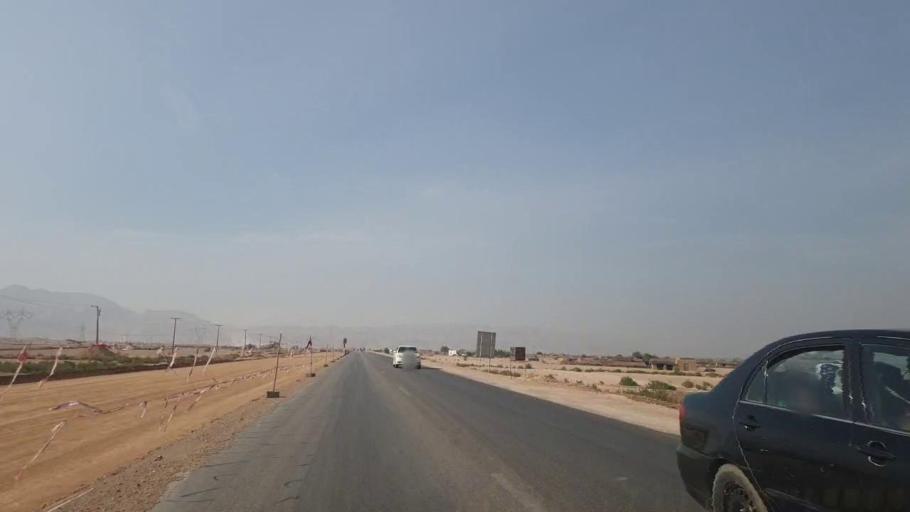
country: PK
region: Sindh
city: Sehwan
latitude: 26.1986
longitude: 67.9413
